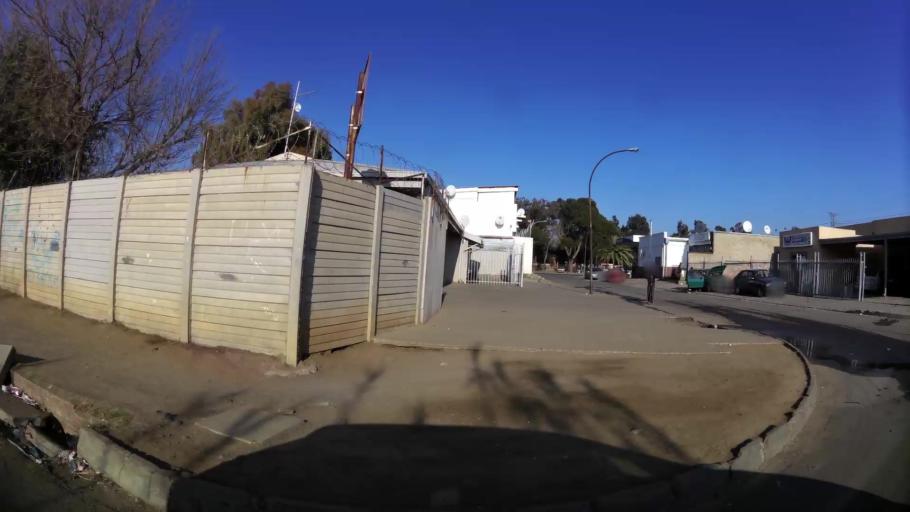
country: ZA
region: Orange Free State
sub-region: Mangaung Metropolitan Municipality
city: Bloemfontein
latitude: -29.1322
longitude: 26.2387
